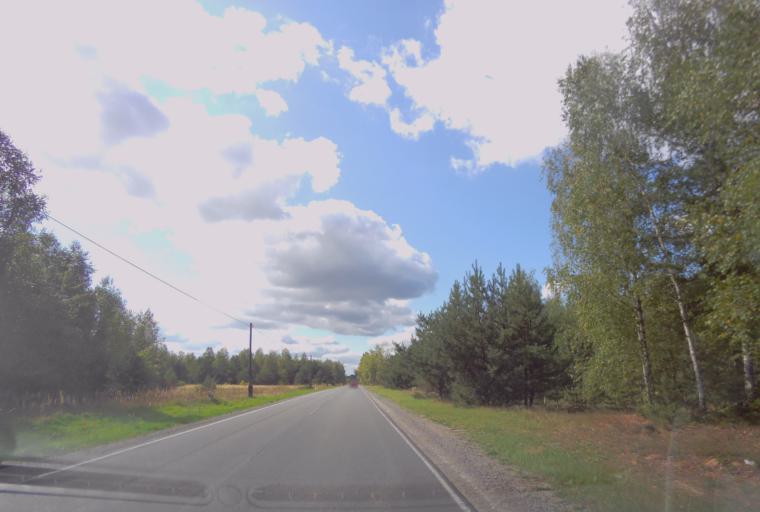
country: PL
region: Subcarpathian Voivodeship
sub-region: Powiat kolbuszowski
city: Majdan Krolewski
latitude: 50.3974
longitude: 21.7817
